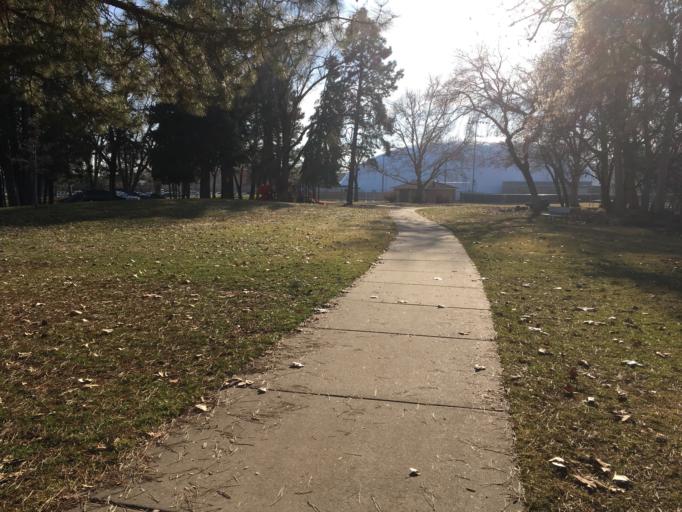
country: US
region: Utah
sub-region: Davis County
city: Layton
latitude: 41.0689
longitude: -111.9605
